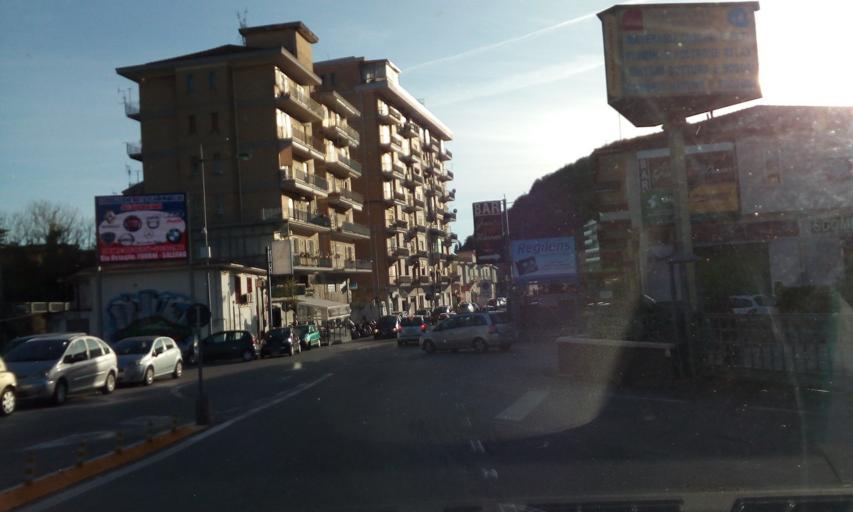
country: IT
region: Campania
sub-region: Provincia di Salerno
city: Capezzano Inferiore
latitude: 40.6972
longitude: 14.7763
